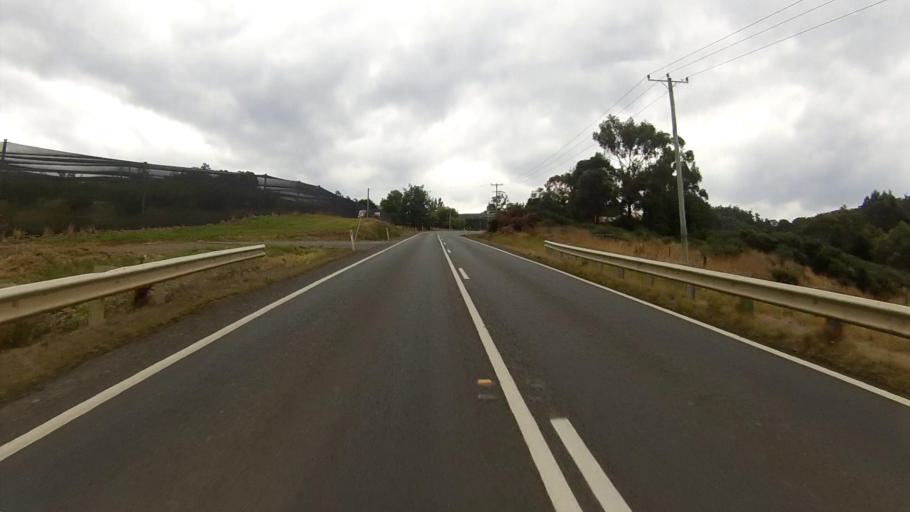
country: AU
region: Tasmania
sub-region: Huon Valley
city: Cygnet
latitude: -43.1314
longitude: 147.0485
